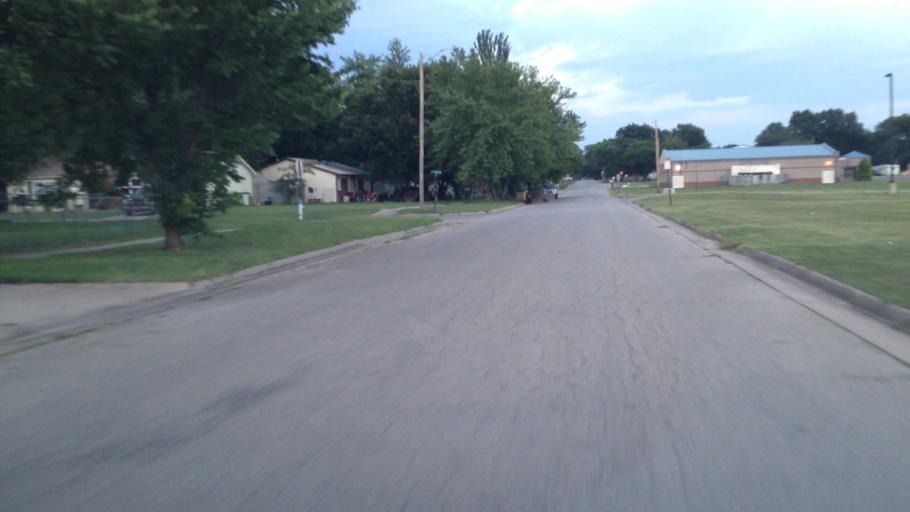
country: US
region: Kansas
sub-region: Montgomery County
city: Independence
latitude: 37.2400
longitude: -95.7139
